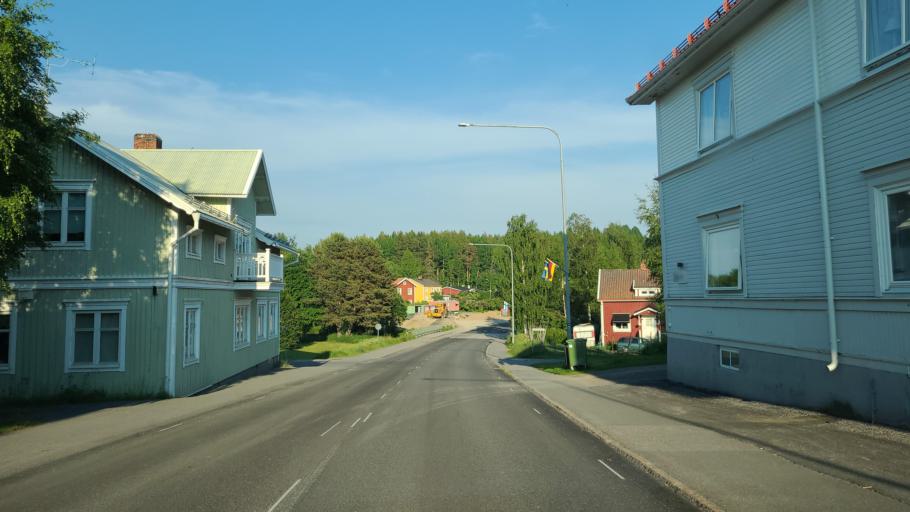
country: SE
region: Vaesterbotten
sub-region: Skelleftea Kommun
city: Burea
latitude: 64.3687
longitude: 21.3190
